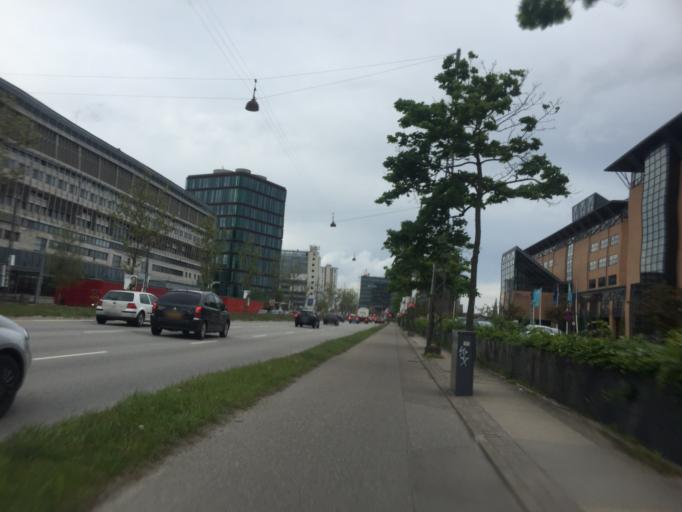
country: DK
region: Capital Region
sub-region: Kobenhavn
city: Copenhagen
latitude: 55.6665
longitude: 12.5689
